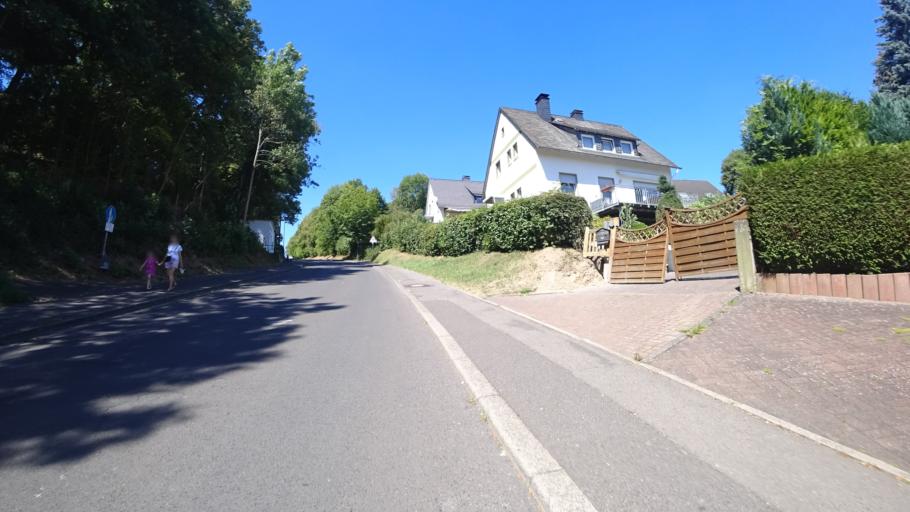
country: DE
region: Rheinland-Pfalz
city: Kumbdchen
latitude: 49.9868
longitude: 7.5207
